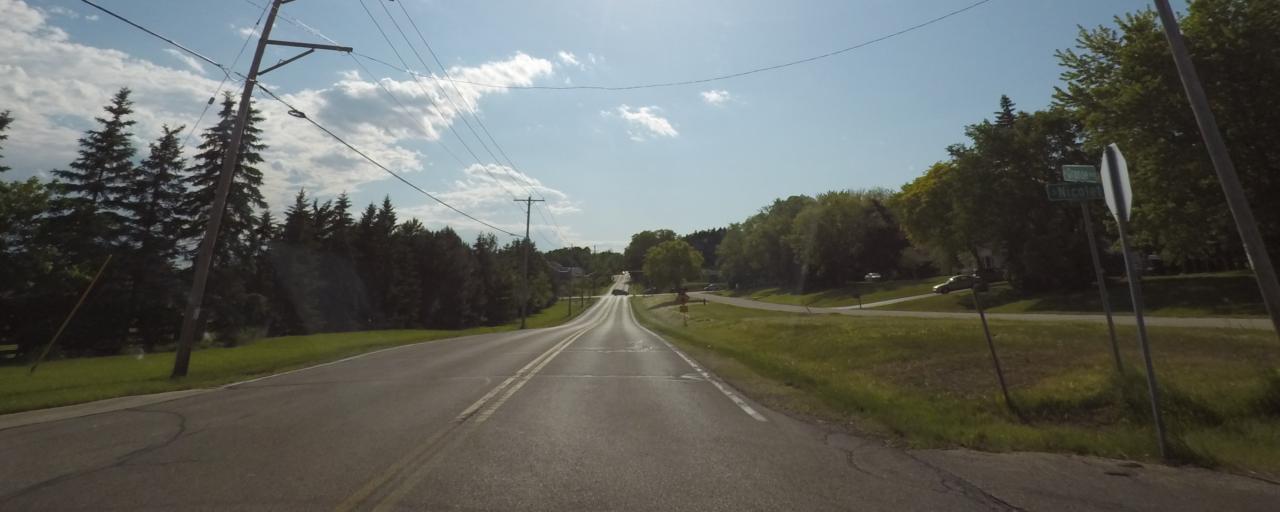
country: US
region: Wisconsin
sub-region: Waukesha County
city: New Berlin
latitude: 42.9444
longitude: -88.0869
